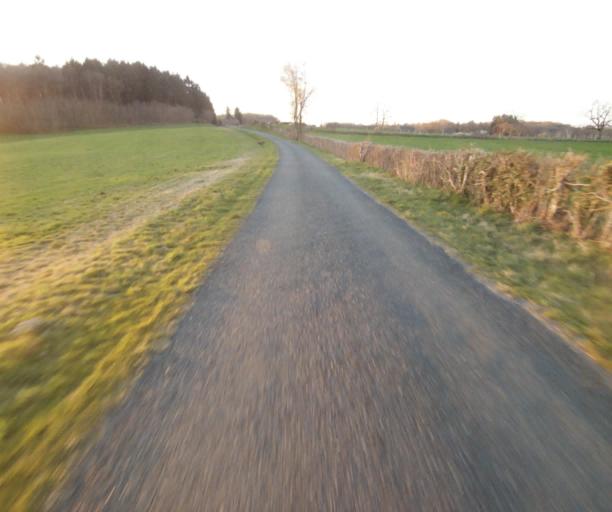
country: FR
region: Limousin
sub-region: Departement de la Correze
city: Uzerche
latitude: 45.3751
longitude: 1.6076
